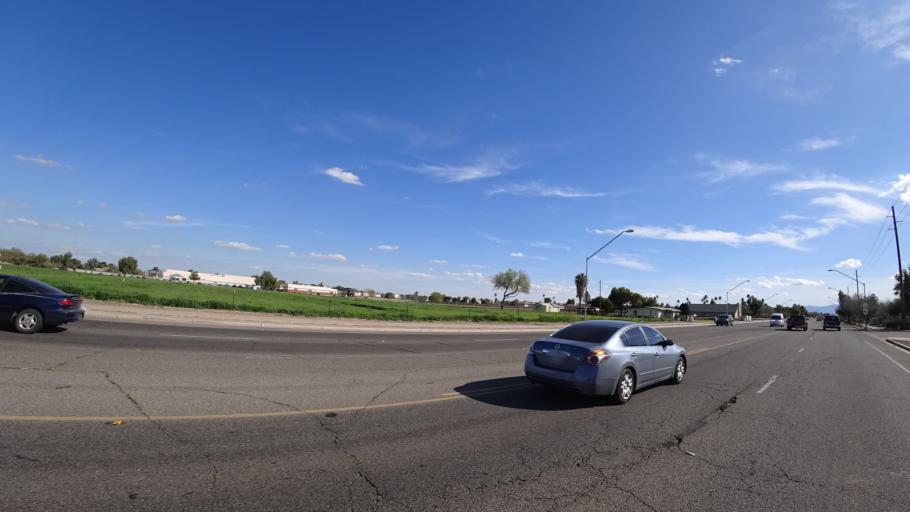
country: US
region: Arizona
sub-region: Maricopa County
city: Glendale
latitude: 33.5441
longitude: -112.2206
